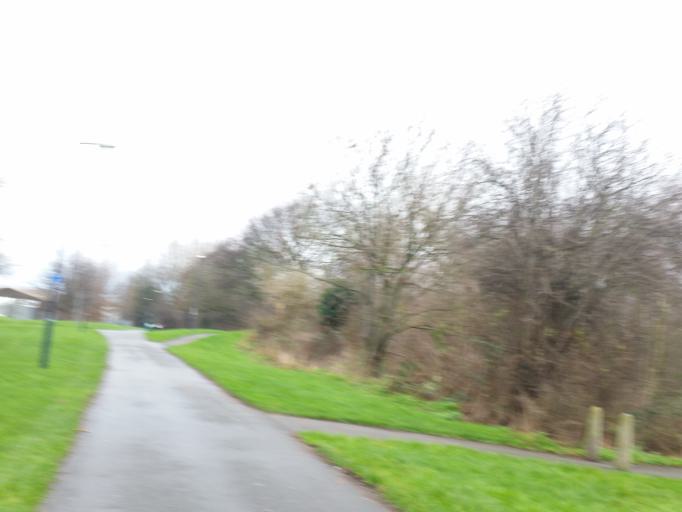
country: GB
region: England
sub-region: Derby
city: Derby
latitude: 52.8986
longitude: -1.4465
